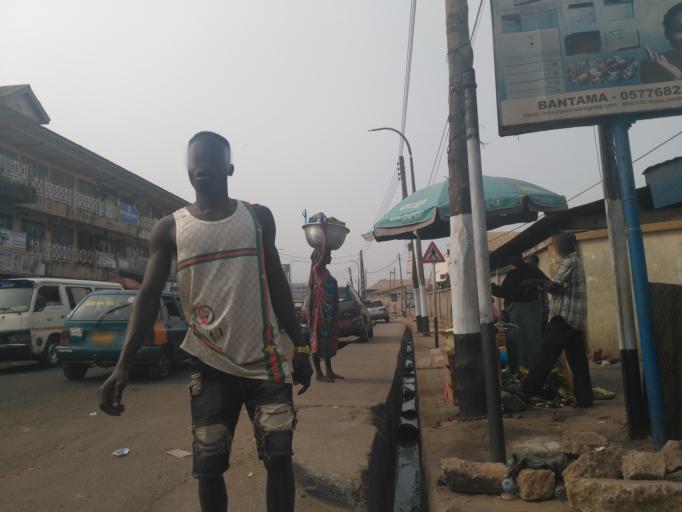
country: GH
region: Ashanti
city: Kumasi
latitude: 6.7036
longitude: -1.6336
